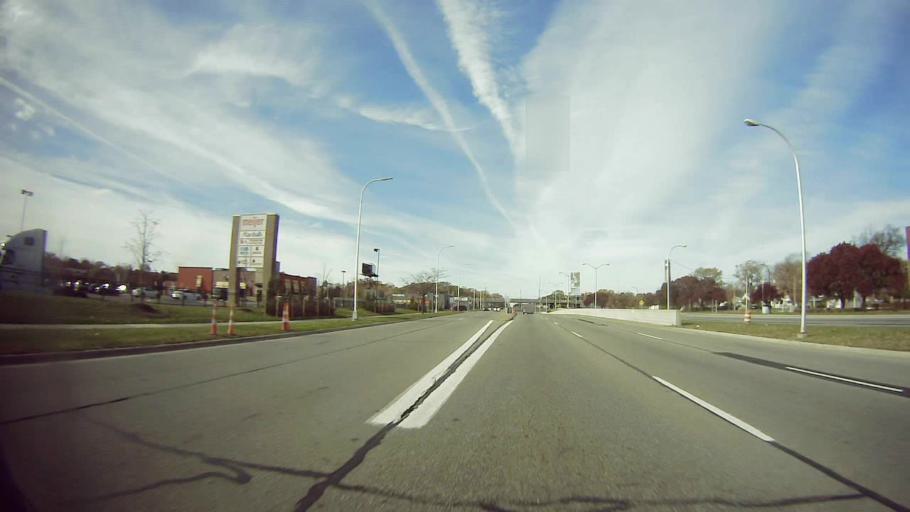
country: US
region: Michigan
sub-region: Oakland County
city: Ferndale
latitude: 42.4466
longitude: -83.1214
